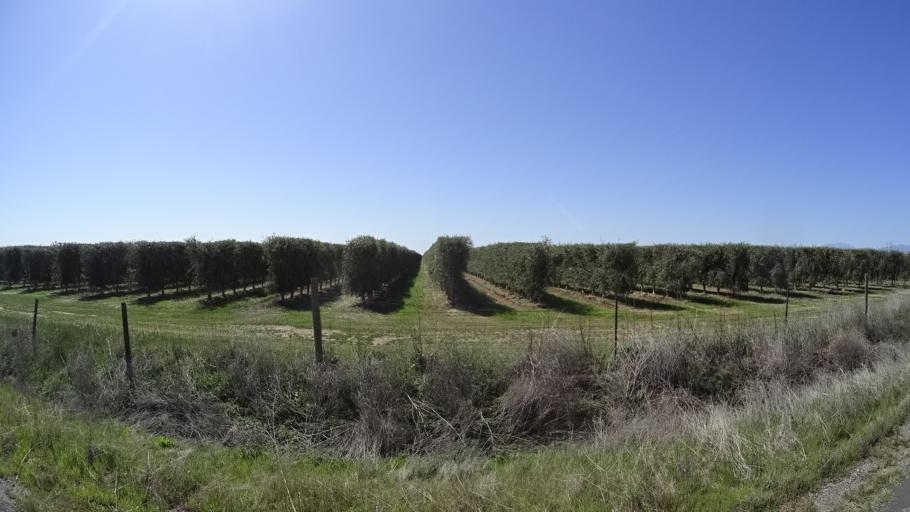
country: US
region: California
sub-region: Glenn County
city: Orland
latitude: 39.6538
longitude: -122.2570
